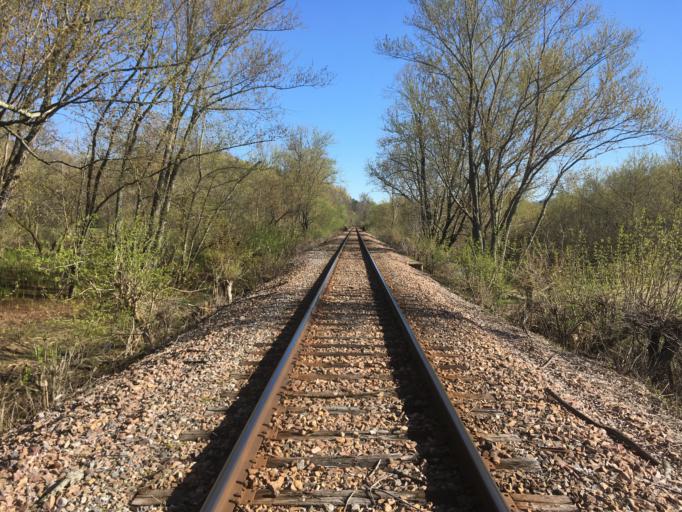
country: US
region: Vermont
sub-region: Rutland County
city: West Rutland
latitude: 43.6452
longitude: -73.0367
